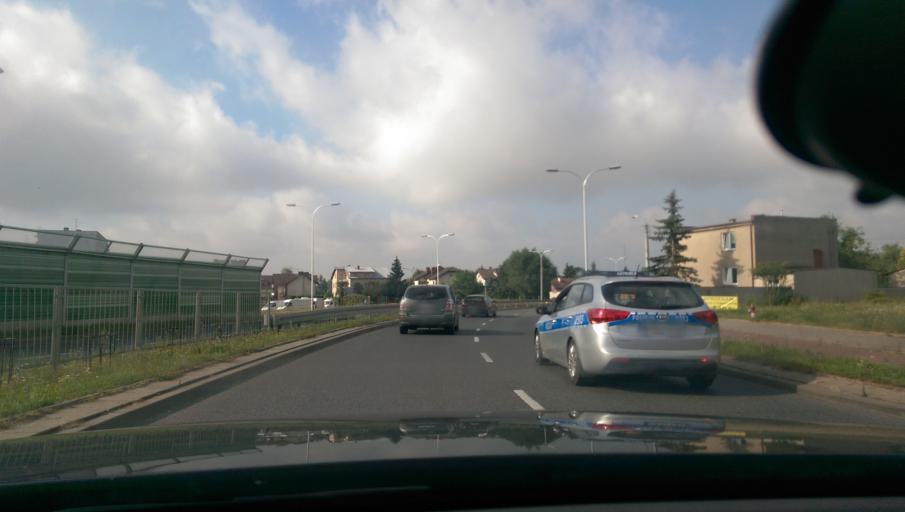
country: PL
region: Masovian Voivodeship
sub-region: Powiat ciechanowski
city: Ciechanow
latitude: 52.8692
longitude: 20.6281
